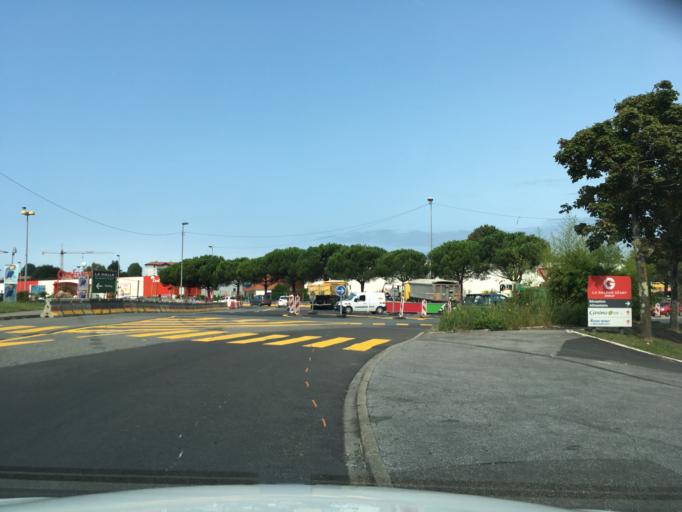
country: FR
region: Aquitaine
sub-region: Departement des Pyrenees-Atlantiques
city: Anglet
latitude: 43.4839
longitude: -1.5042
